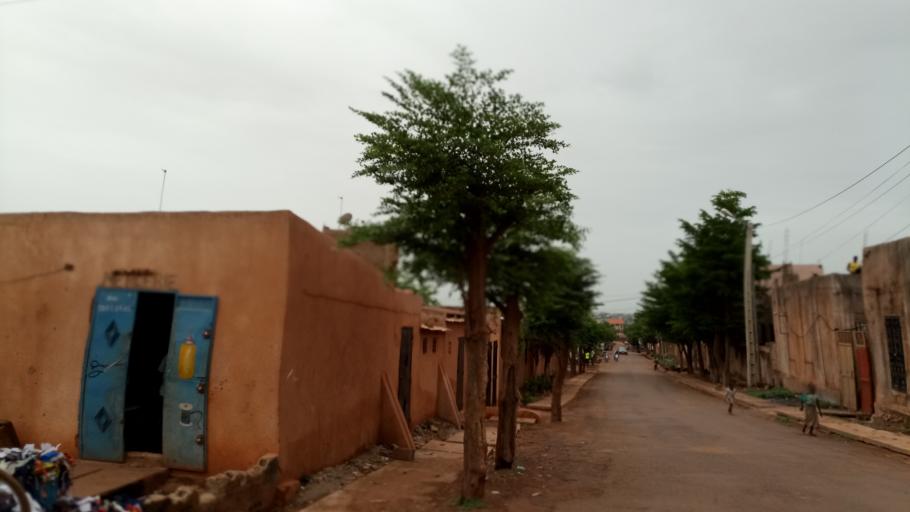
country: ML
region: Bamako
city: Bamako
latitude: 12.5887
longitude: -7.9933
